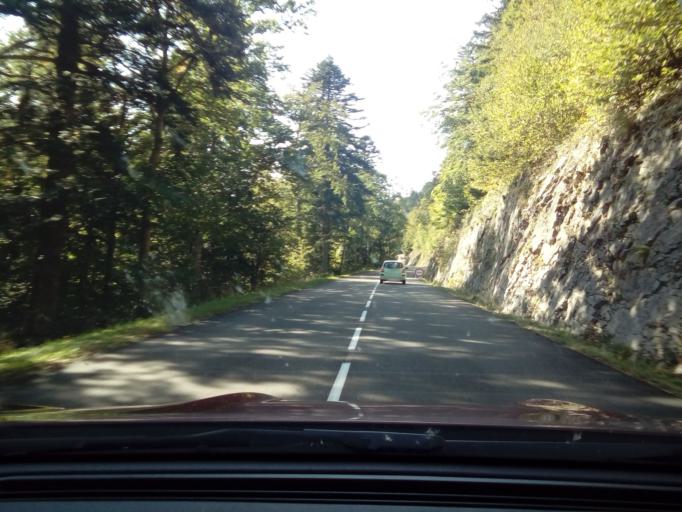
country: FR
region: Rhone-Alpes
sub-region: Departement de la Drome
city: Die
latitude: 44.8502
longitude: 5.4050
